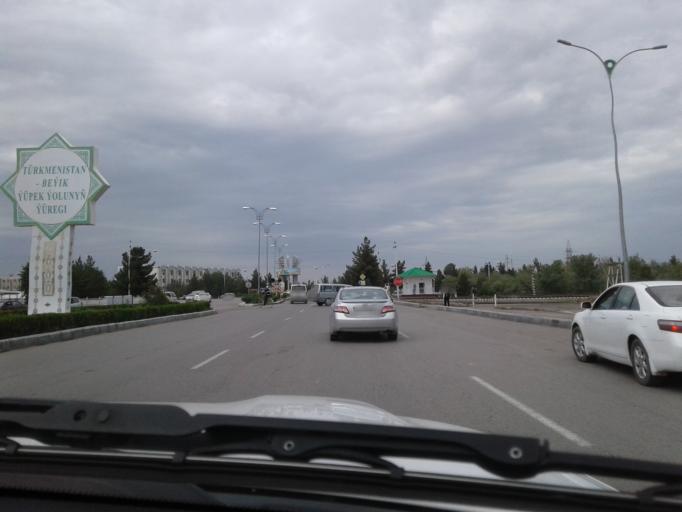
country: TM
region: Mary
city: Mary
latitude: 37.5950
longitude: 61.8772
